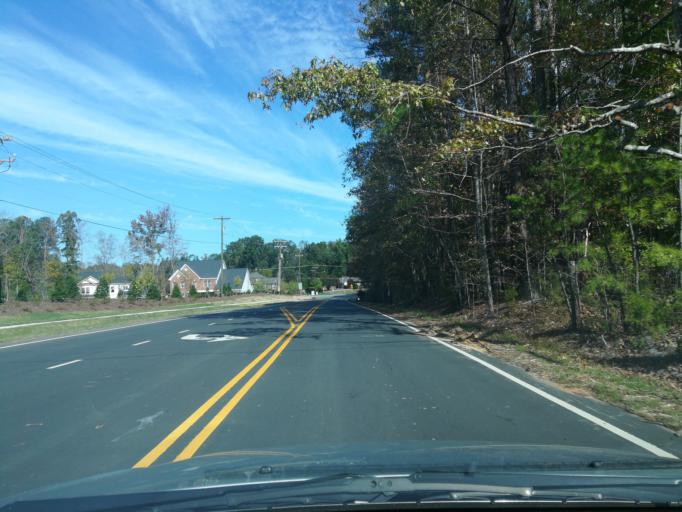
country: US
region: North Carolina
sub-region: Durham County
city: Durham
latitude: 35.9739
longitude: -78.9758
